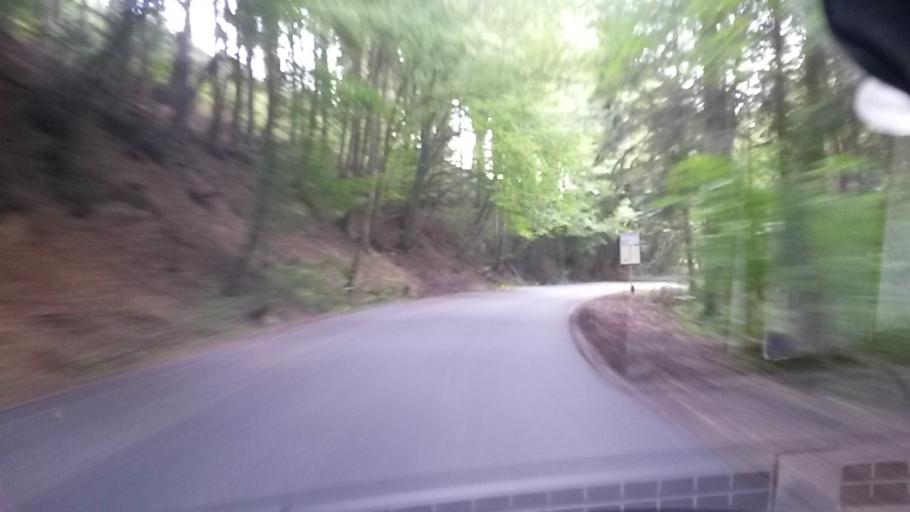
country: DE
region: North Rhine-Westphalia
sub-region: Regierungsbezirk Koln
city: Engelskirchen
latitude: 50.9792
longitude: 7.4357
